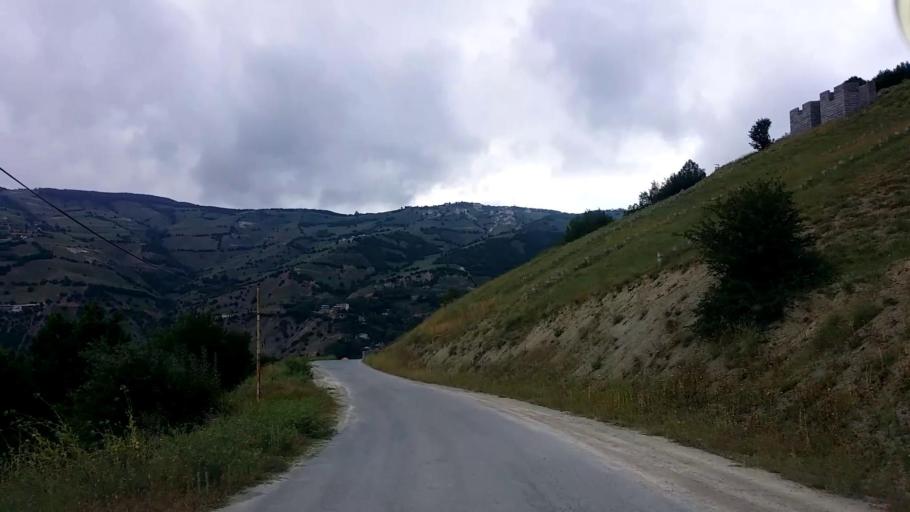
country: IR
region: Mazandaran
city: Chalus
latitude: 36.5526
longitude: 51.2841
